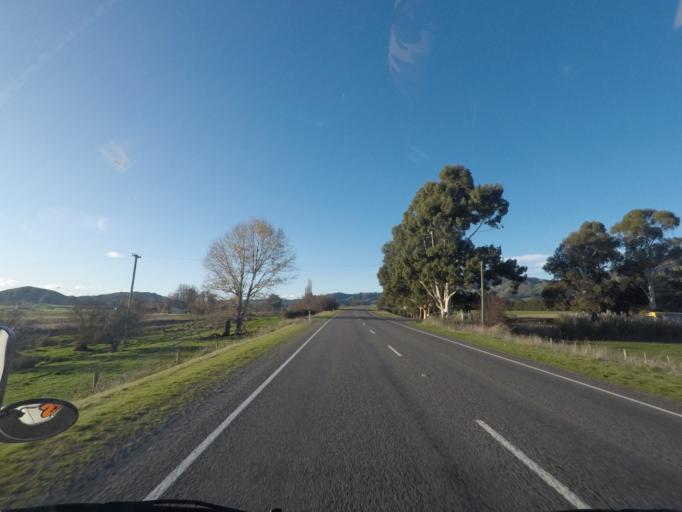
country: NZ
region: Canterbury
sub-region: Kaikoura District
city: Kaikoura
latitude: -42.7095
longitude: 173.2936
